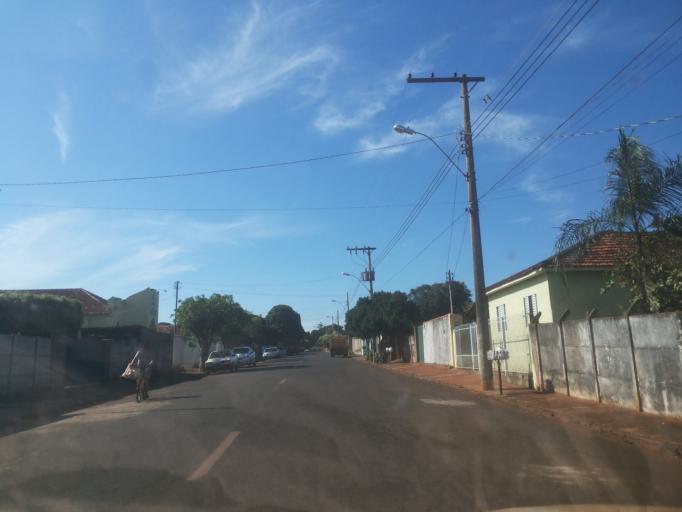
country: BR
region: Minas Gerais
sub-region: Centralina
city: Centralina
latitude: -18.7205
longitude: -49.2016
